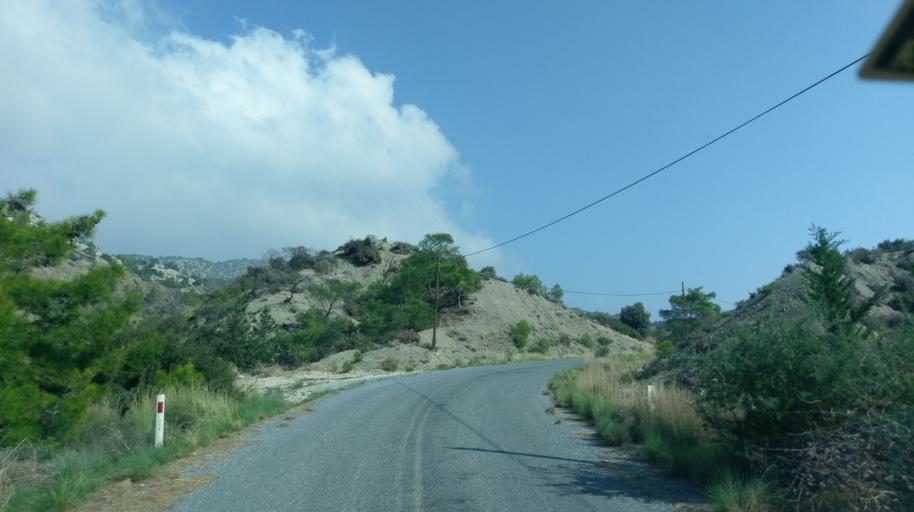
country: CY
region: Ammochostos
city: Lefkonoiko
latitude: 35.3205
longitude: 33.6557
